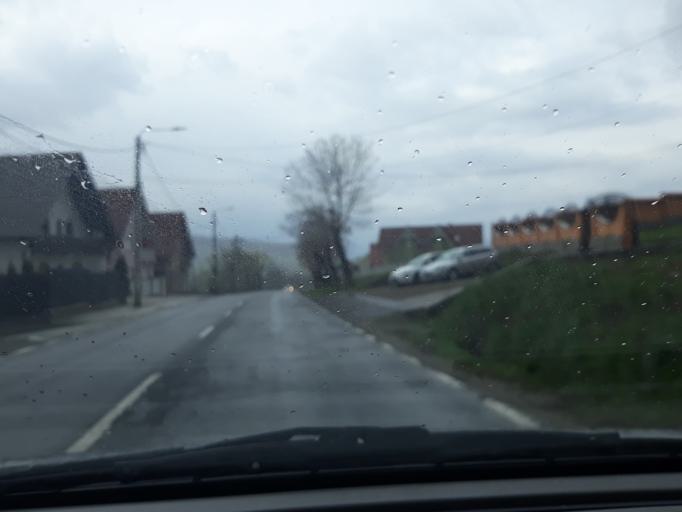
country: RO
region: Harghita
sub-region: Comuna Corund
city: Corund
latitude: 46.4788
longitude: 25.1743
